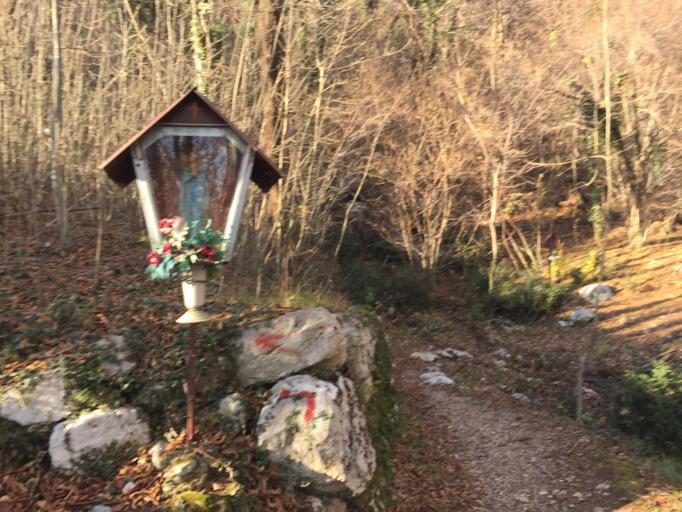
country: IT
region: Friuli Venezia Giulia
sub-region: Provincia di Udine
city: Trasaghis
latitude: 46.2898
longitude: 13.0917
